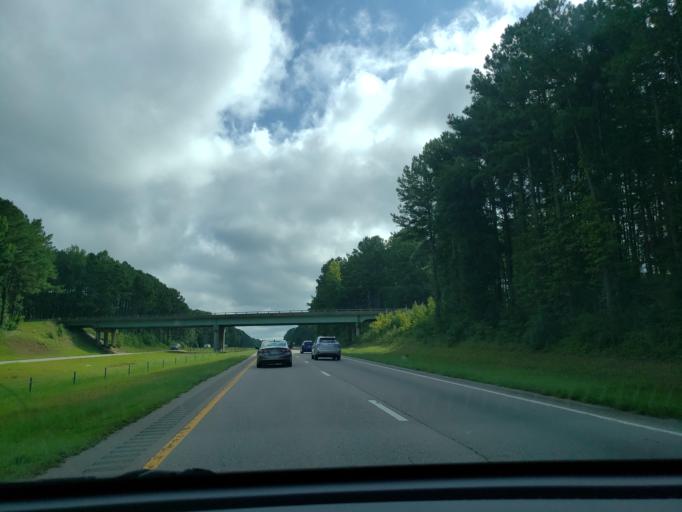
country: US
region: North Carolina
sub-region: Wake County
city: Zebulon
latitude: 35.8781
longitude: -78.2236
